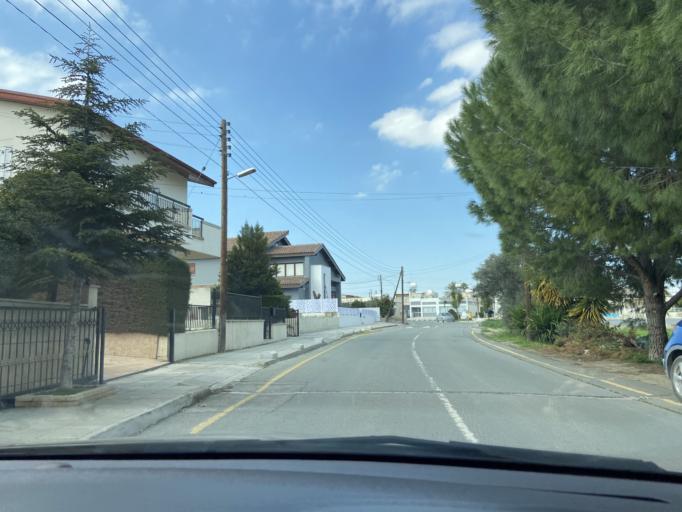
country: CY
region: Lefkosia
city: Alampra
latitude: 35.0192
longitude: 33.3902
